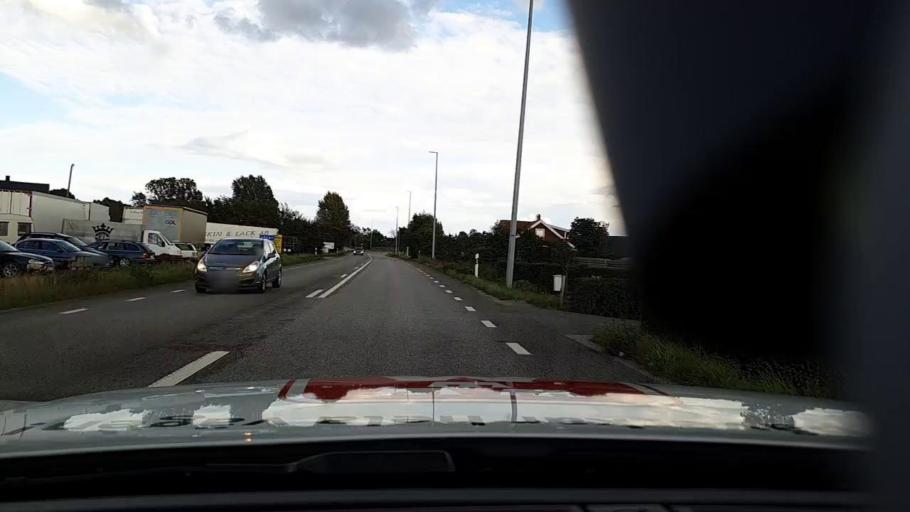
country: SE
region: Blekinge
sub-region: Solvesborgs Kommun
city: Soelvesborg
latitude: 56.0493
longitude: 14.6555
